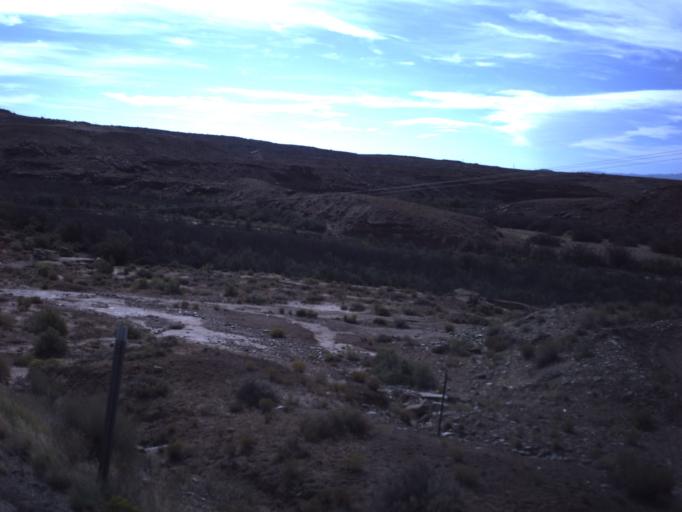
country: US
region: Utah
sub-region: San Juan County
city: Blanding
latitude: 37.3087
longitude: -109.2981
